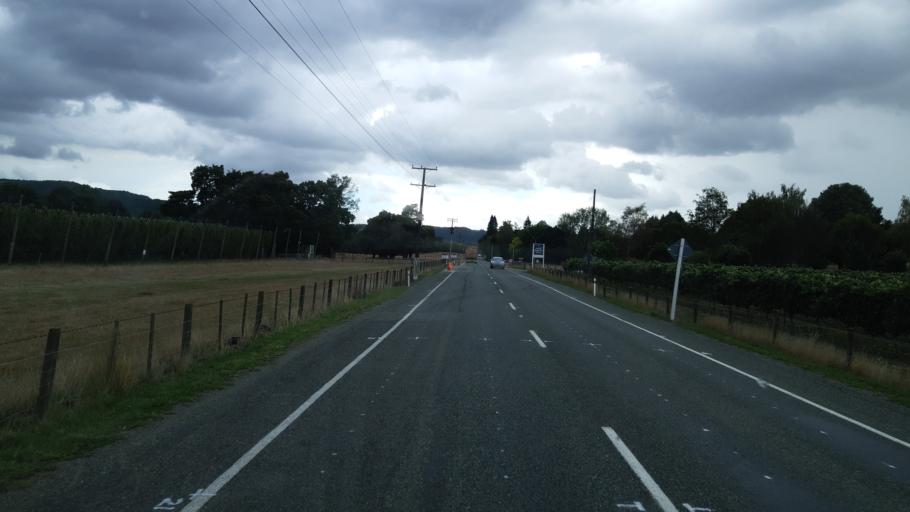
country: NZ
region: Tasman
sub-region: Tasman District
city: Wakefield
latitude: -41.4188
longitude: 173.0081
